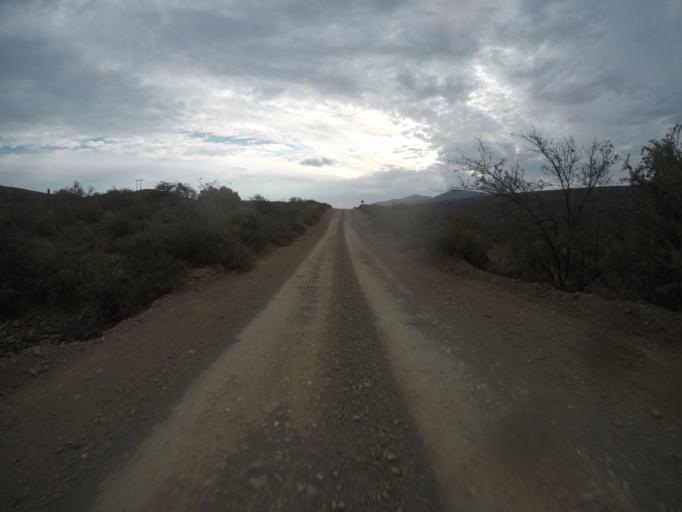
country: ZA
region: Eastern Cape
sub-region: Cacadu District Municipality
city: Willowmore
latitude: -33.4888
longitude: 23.5593
